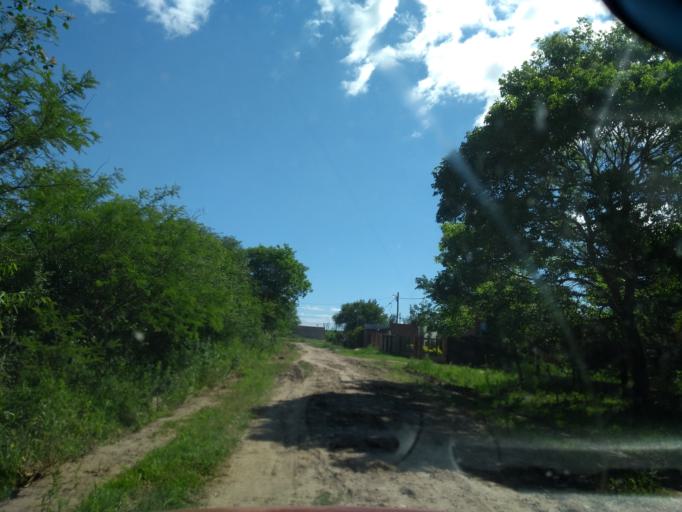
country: AR
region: Chaco
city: Resistencia
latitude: -27.4203
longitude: -58.9470
